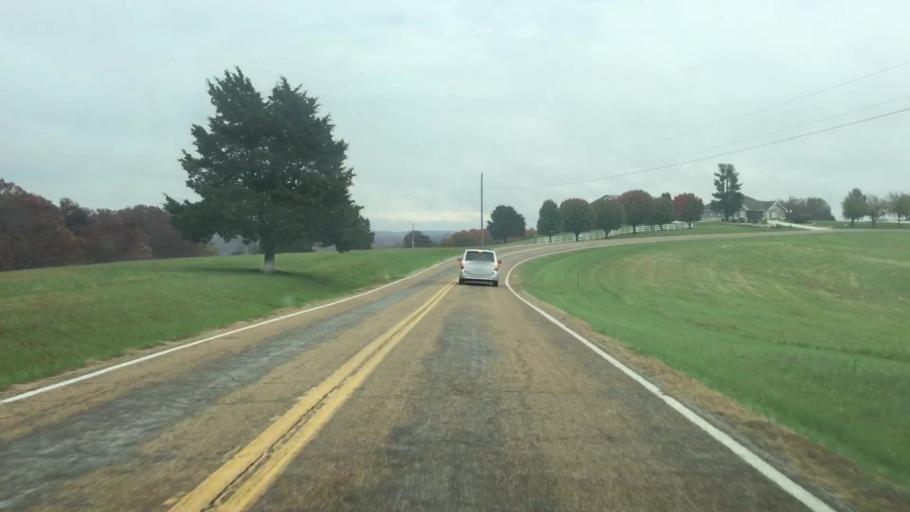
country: US
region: Missouri
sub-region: Callaway County
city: Fulton
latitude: 38.7409
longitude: -91.7076
